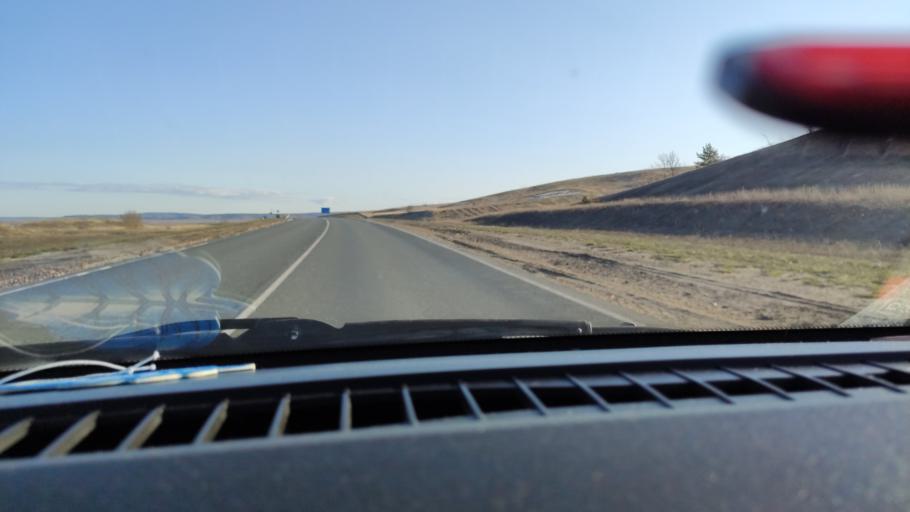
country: RU
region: Saratov
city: Alekseyevka
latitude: 52.3414
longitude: 47.9352
